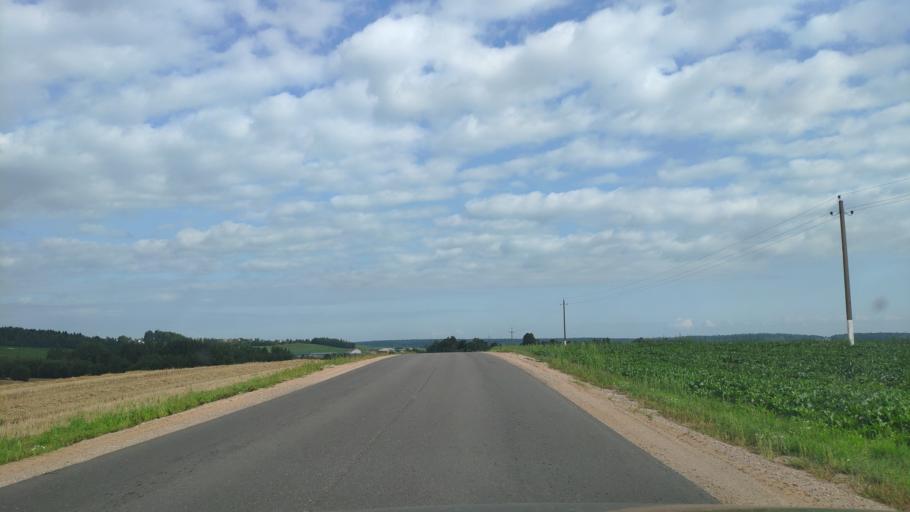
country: BY
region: Minsk
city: Khatsyezhyna
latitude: 53.8458
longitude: 27.3134
